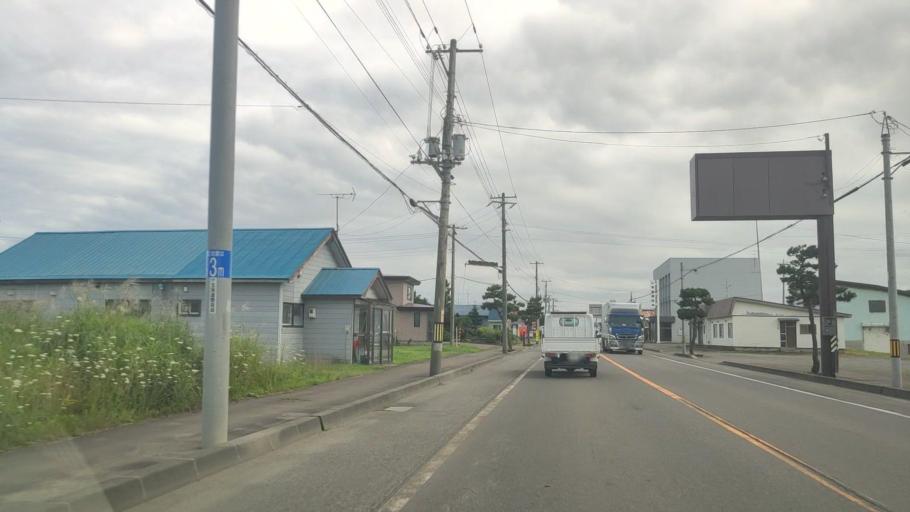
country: JP
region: Hokkaido
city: Niseko Town
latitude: 42.4394
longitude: 140.3242
